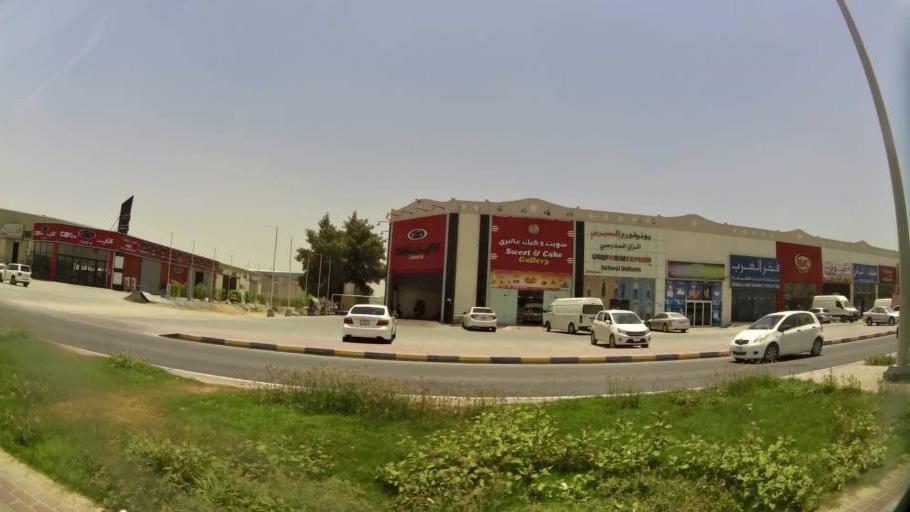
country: AE
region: Ajman
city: Ajman
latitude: 25.4034
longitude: 55.4983
